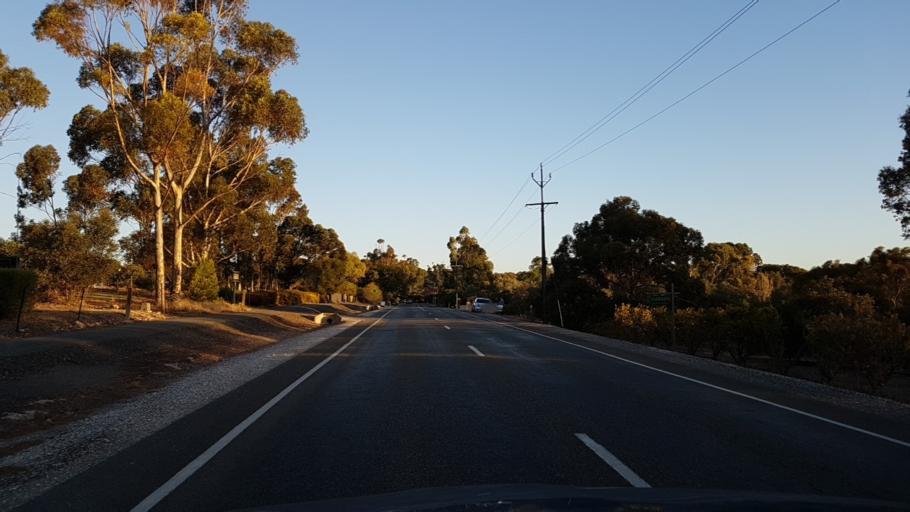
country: AU
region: South Australia
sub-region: Wakefield
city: Balaklava
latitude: -34.1427
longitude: 138.6885
